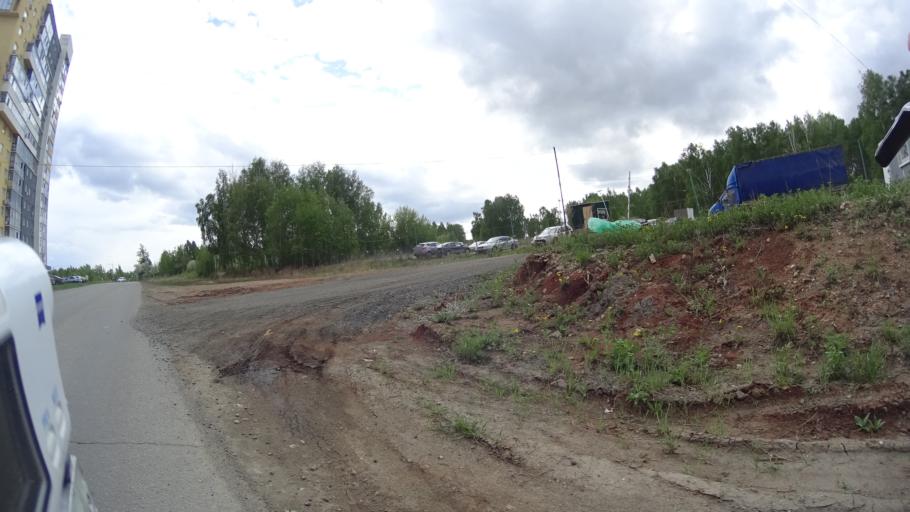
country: RU
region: Chelyabinsk
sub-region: Gorod Chelyabinsk
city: Chelyabinsk
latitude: 55.1609
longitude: 61.2856
